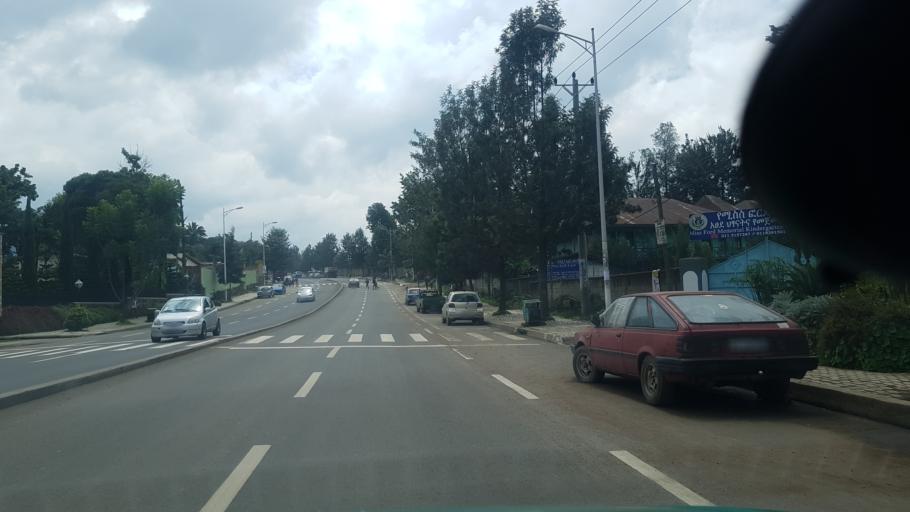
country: ET
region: Adis Abeba
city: Addis Ababa
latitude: 9.0207
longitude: 38.7719
